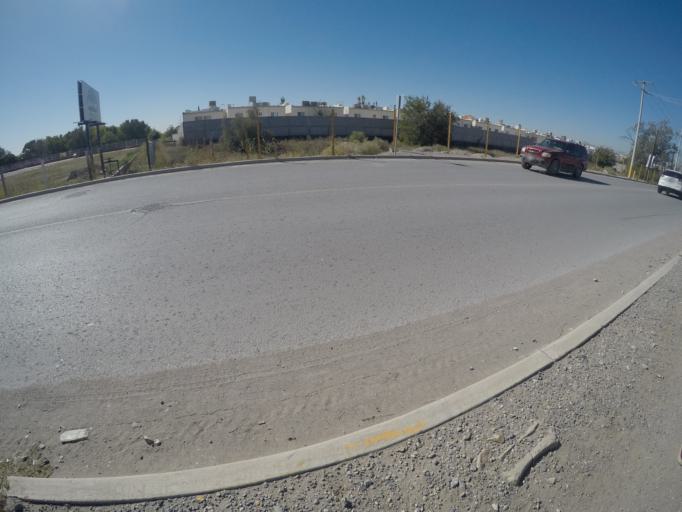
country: US
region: Texas
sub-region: El Paso County
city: Socorro
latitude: 31.6909
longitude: -106.3577
